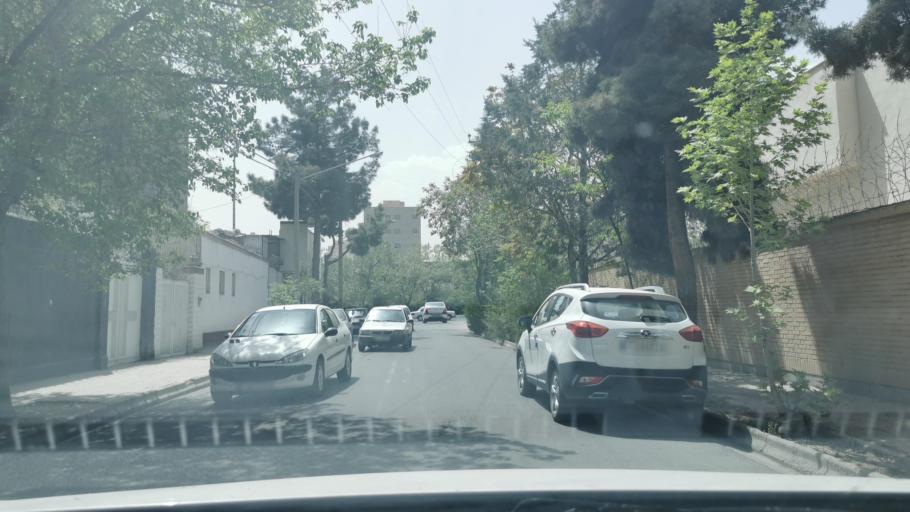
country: IR
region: Razavi Khorasan
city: Mashhad
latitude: 36.3348
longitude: 59.4808
